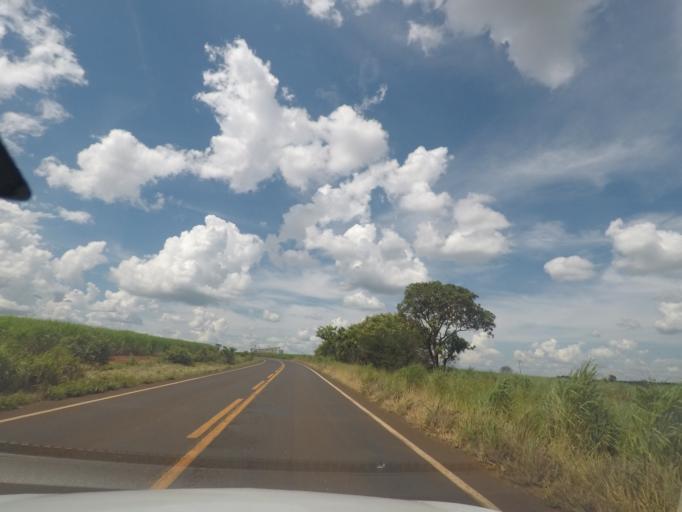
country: BR
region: Minas Gerais
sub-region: Conceicao Das Alagoas
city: Conceicao das Alagoas
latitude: -19.8129
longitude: -48.5850
